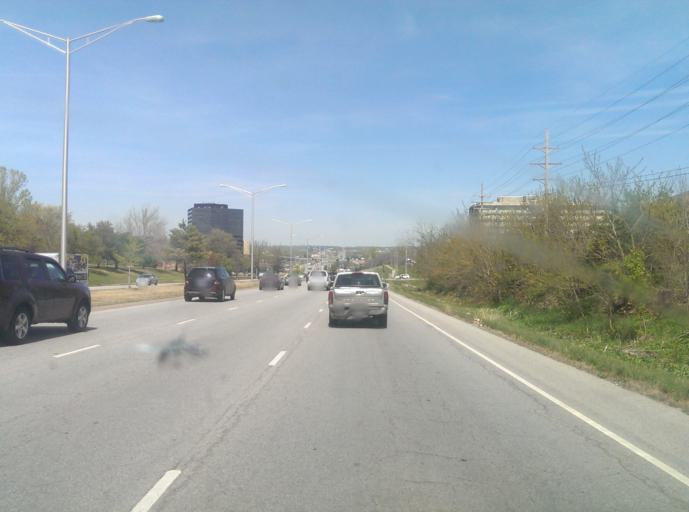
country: US
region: Kansas
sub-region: Johnson County
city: Overland Park
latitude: 38.9205
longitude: -94.6673
